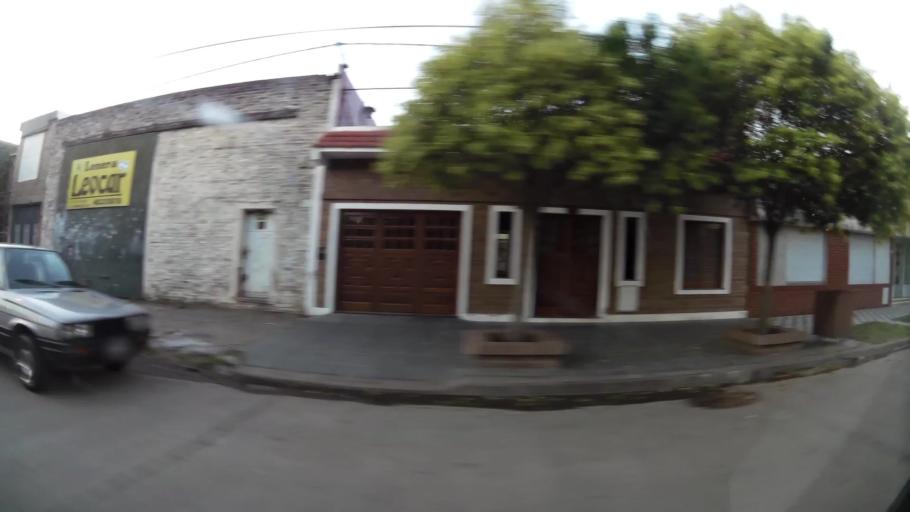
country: AR
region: Cordoba
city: Villa Maria
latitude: -32.4097
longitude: -63.2575
